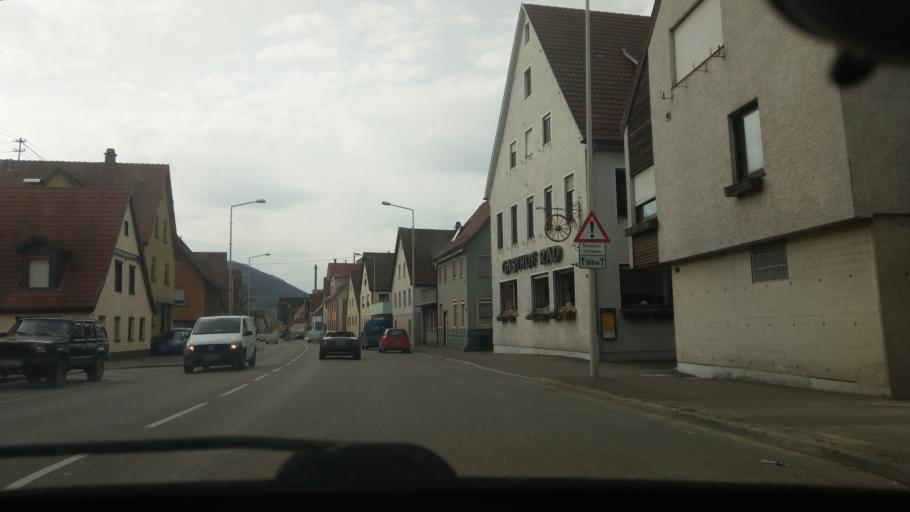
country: DE
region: Baden-Wuerttemberg
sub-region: Regierungsbezirk Stuttgart
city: Geislingen an der Steige
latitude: 48.6270
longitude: 9.8218
